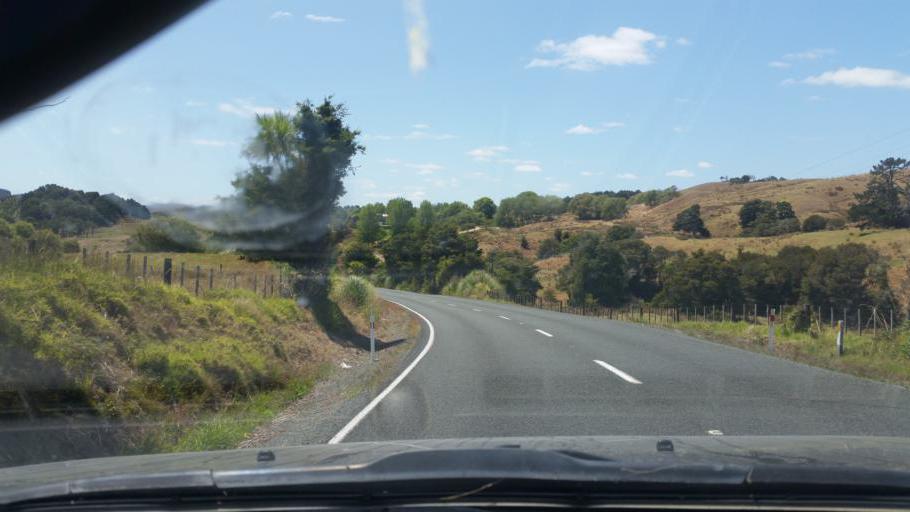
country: NZ
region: Auckland
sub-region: Auckland
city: Wellsford
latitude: -36.1359
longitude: 174.3235
